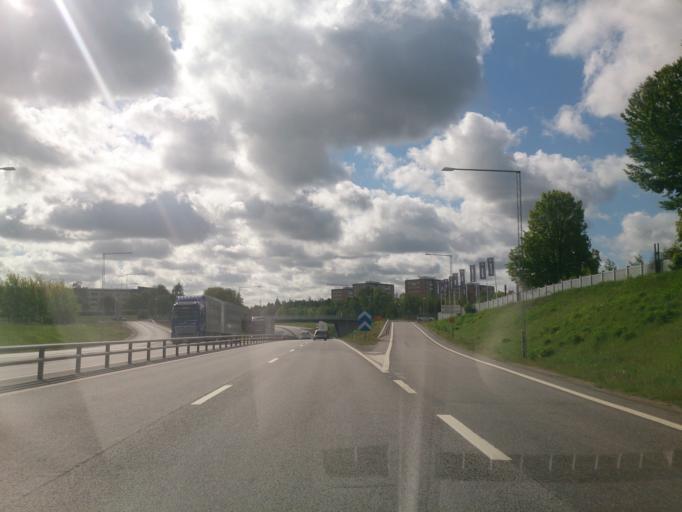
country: SE
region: OEstergoetland
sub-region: Norrkopings Kommun
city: Norrkoping
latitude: 58.5788
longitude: 16.1577
